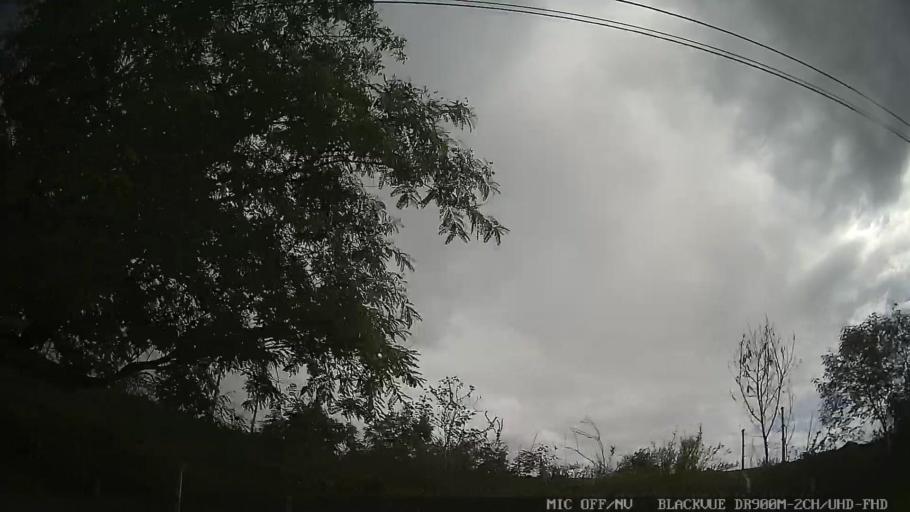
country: BR
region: Sao Paulo
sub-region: Jaguariuna
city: Jaguariuna
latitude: -22.6910
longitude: -46.9946
